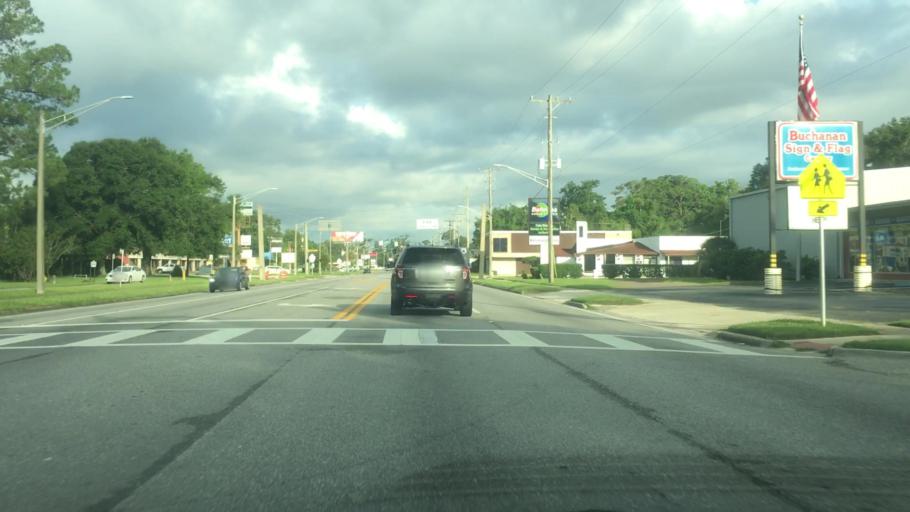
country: US
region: Florida
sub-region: Duval County
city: Jacksonville
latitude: 30.2821
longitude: -81.5886
